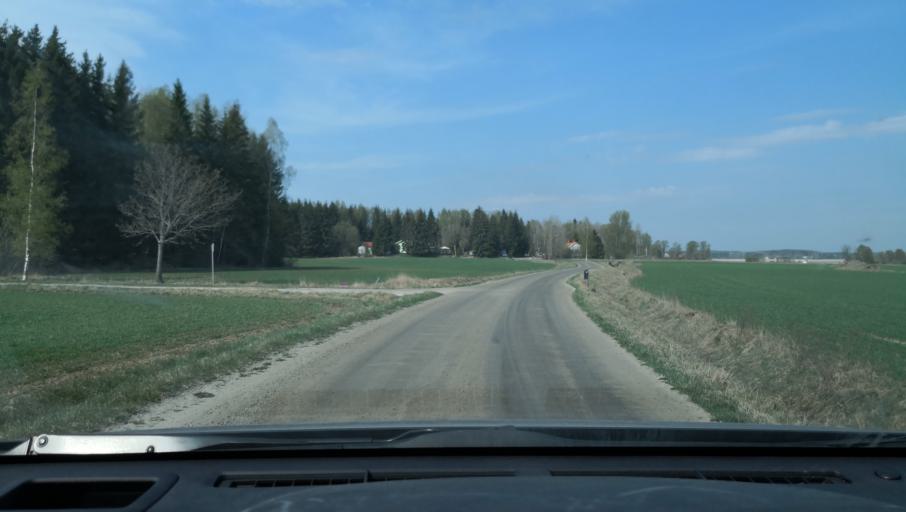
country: SE
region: Vaestmanland
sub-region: Vasteras
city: Skultuna
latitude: 59.7660
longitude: 16.4566
